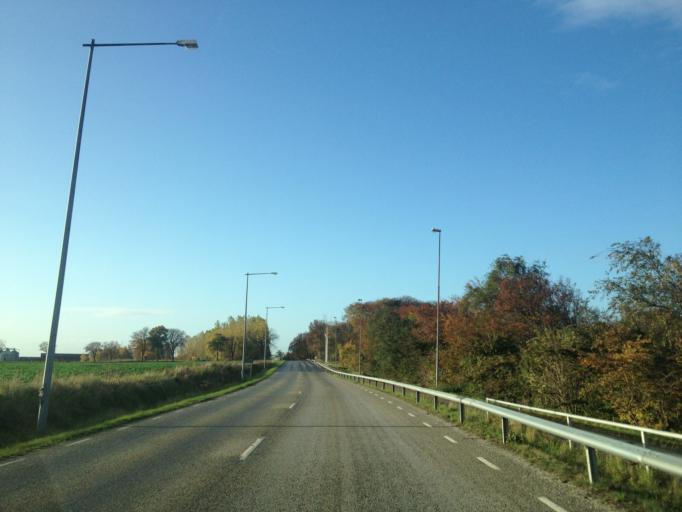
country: SE
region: Skane
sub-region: Lomma Kommun
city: Lomma
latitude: 55.6591
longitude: 13.0586
